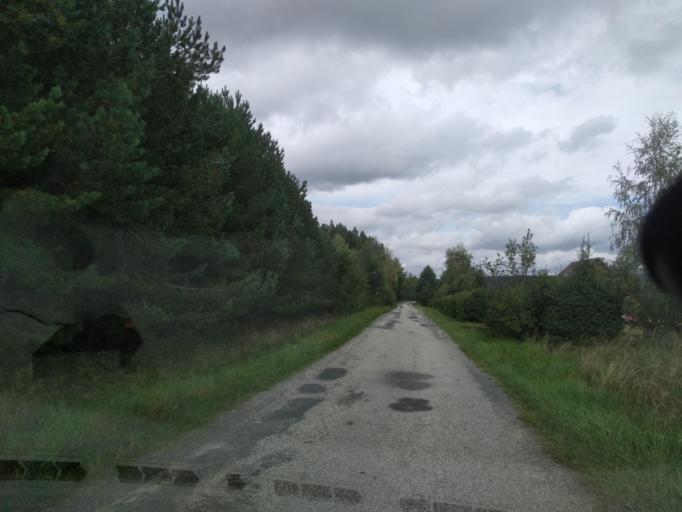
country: PL
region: Lesser Poland Voivodeship
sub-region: Powiat gorlicki
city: Uscie Gorlickie
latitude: 49.5396
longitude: 21.1801
